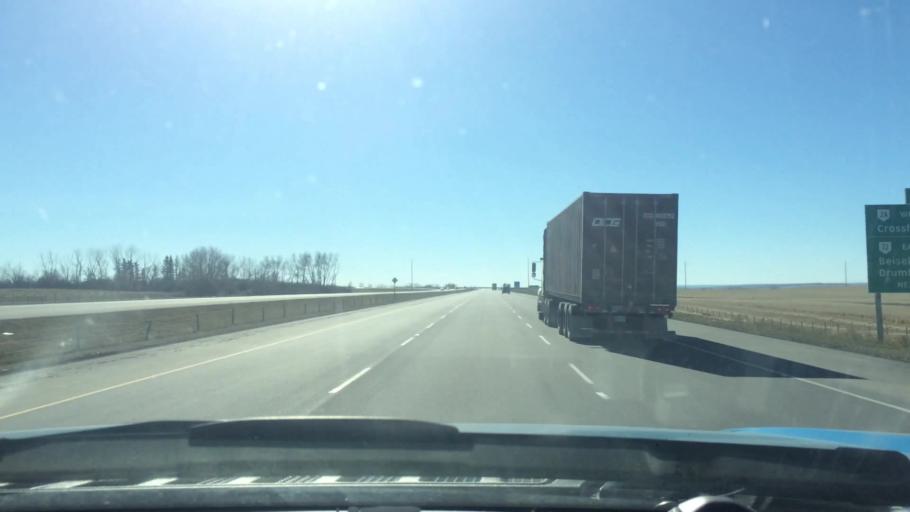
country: CA
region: Alberta
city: Crossfield
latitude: 51.4017
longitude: -114.0021
